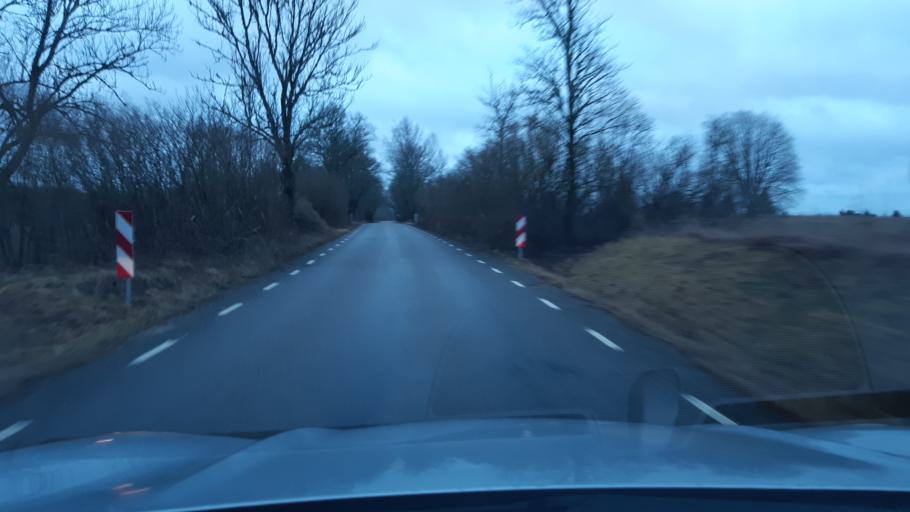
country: EE
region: Raplamaa
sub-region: Rapla vald
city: Rapla
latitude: 58.9918
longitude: 24.7245
